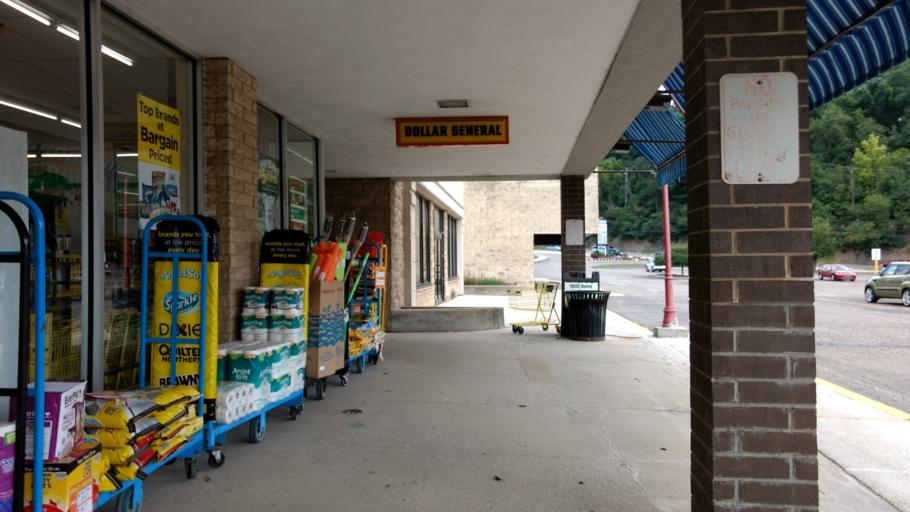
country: US
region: Pennsylvania
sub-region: Westmoreland County
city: Murrysville
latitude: 40.4278
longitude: -79.7076
